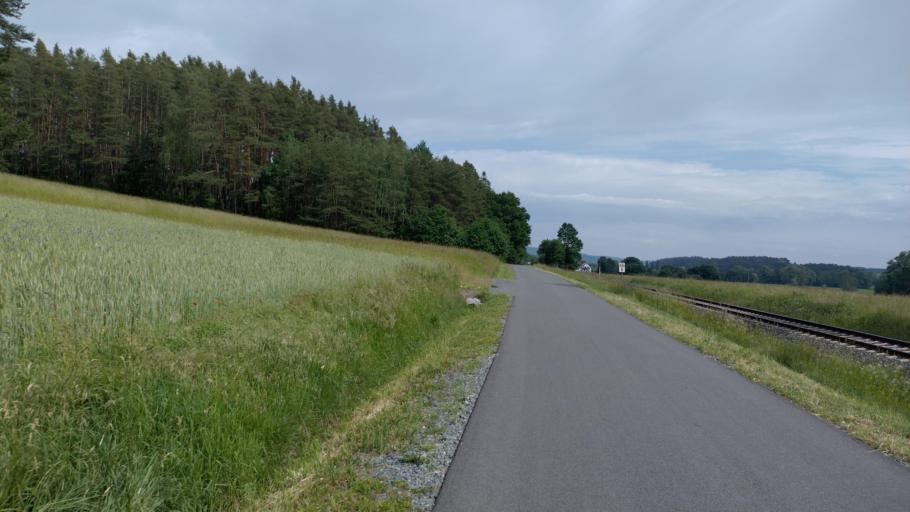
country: DE
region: Bavaria
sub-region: Upper Franconia
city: Harsdorf
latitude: 50.0145
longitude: 11.5812
